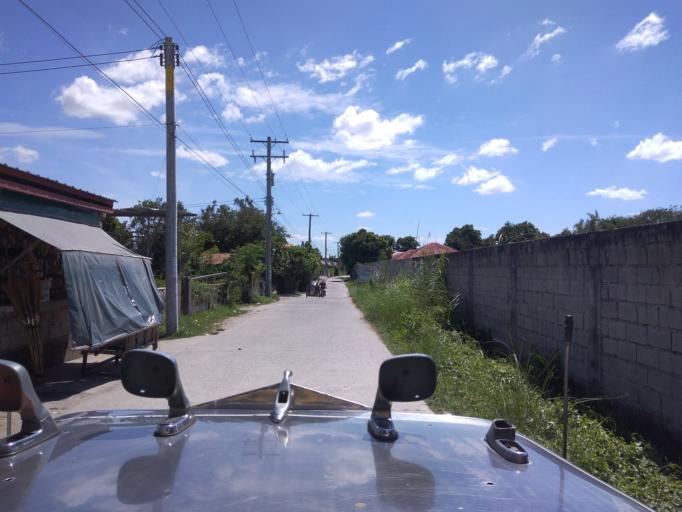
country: PH
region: Central Luzon
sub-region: Province of Pampanga
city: Magliman
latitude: 15.0517
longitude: 120.6412
